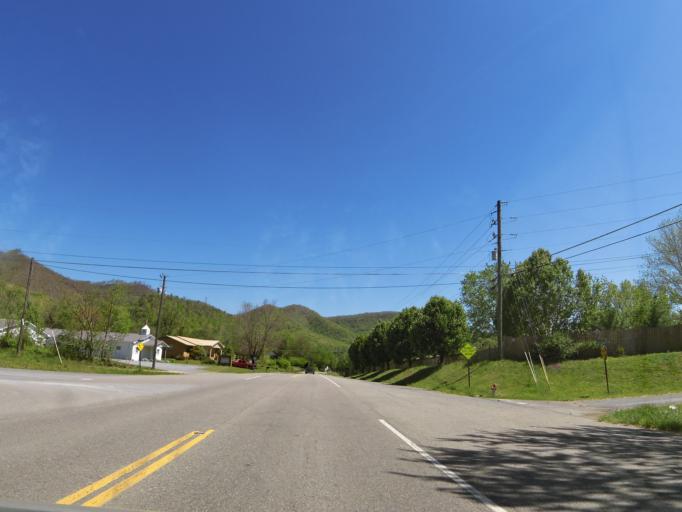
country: US
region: Tennessee
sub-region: Unicoi County
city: Erwin
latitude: 36.1774
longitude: -82.4540
